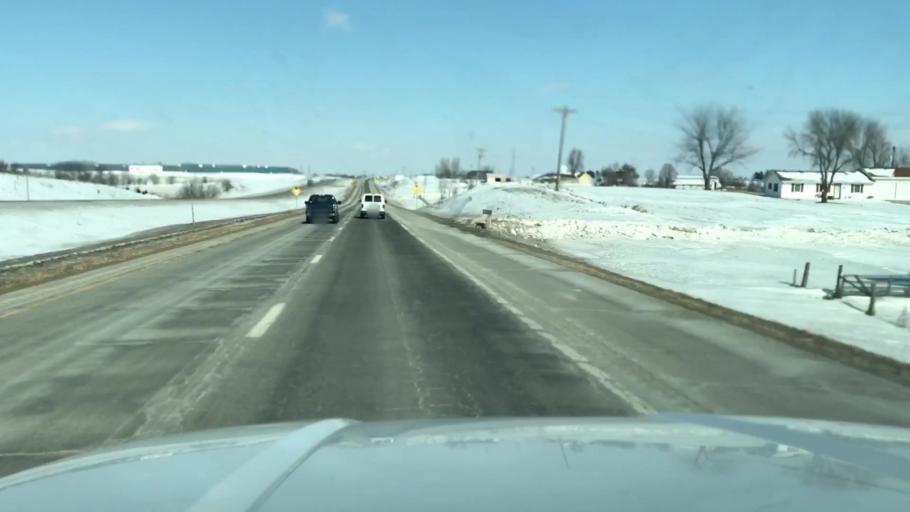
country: US
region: Missouri
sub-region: Nodaway County
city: Maryville
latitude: 40.3018
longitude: -94.8745
